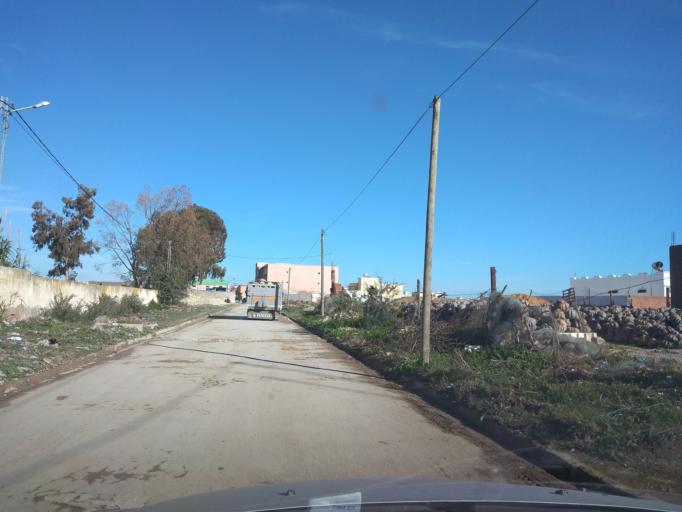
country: TN
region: Ariana
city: Qal'at al Andalus
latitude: 37.0576
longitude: 10.1206
